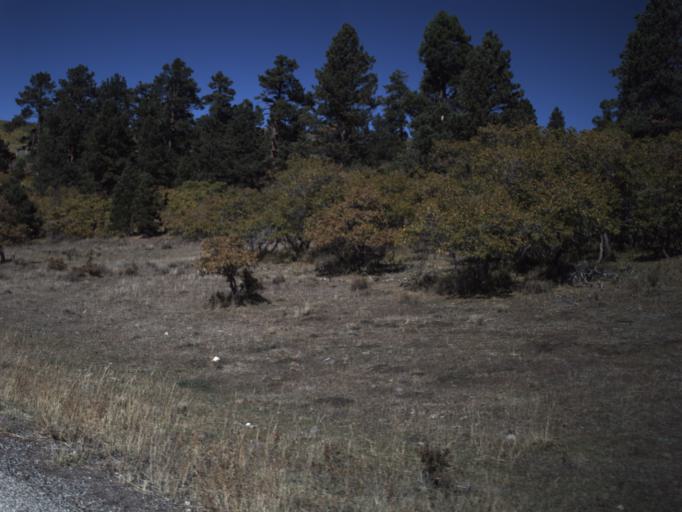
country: US
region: Utah
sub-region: Wayne County
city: Loa
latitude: 38.0085
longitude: -111.3972
